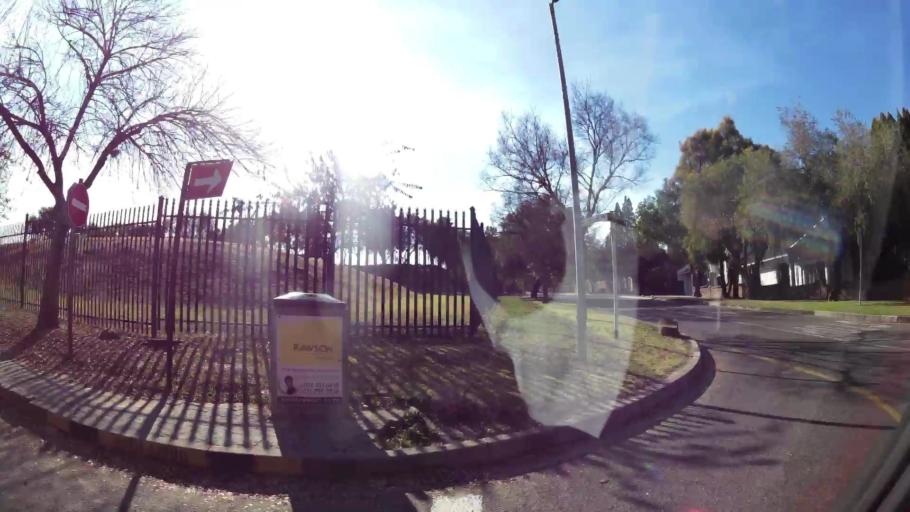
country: ZA
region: Gauteng
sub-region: City of Johannesburg Metropolitan Municipality
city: Roodepoort
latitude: -26.1005
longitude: 27.9567
